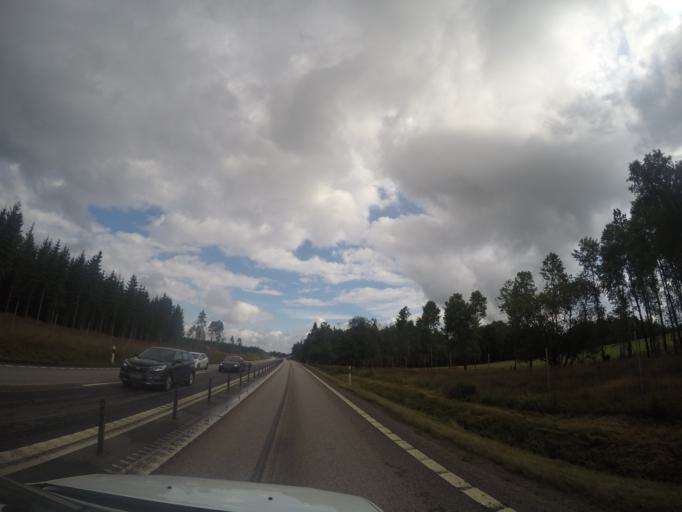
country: SE
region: Kronoberg
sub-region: Ljungby Kommun
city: Ljungby
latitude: 56.8043
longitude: 13.8985
